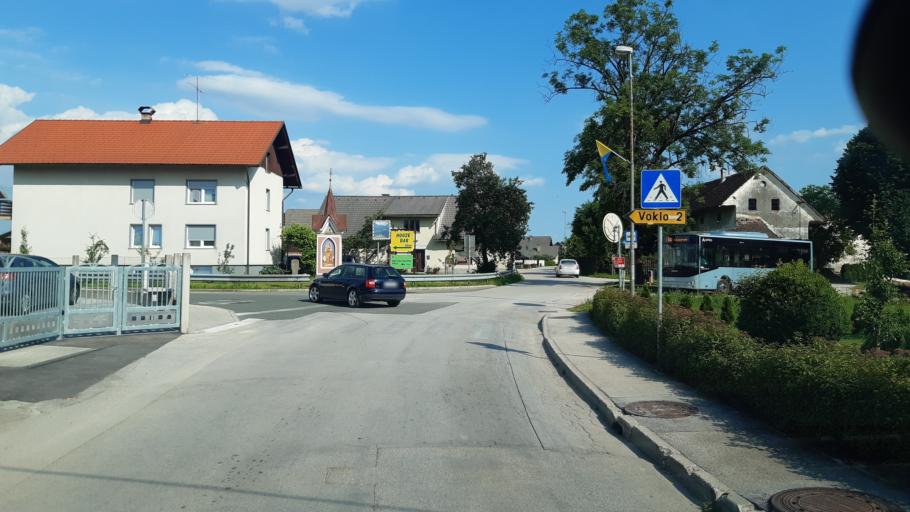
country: SI
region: Sencur
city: Hrastje
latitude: 46.2122
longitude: 14.3963
